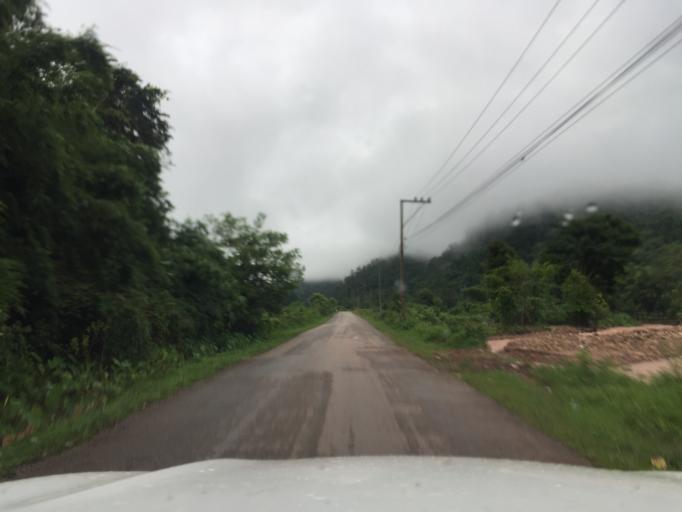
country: LA
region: Oudomxai
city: Muang La
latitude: 20.8350
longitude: 102.1012
